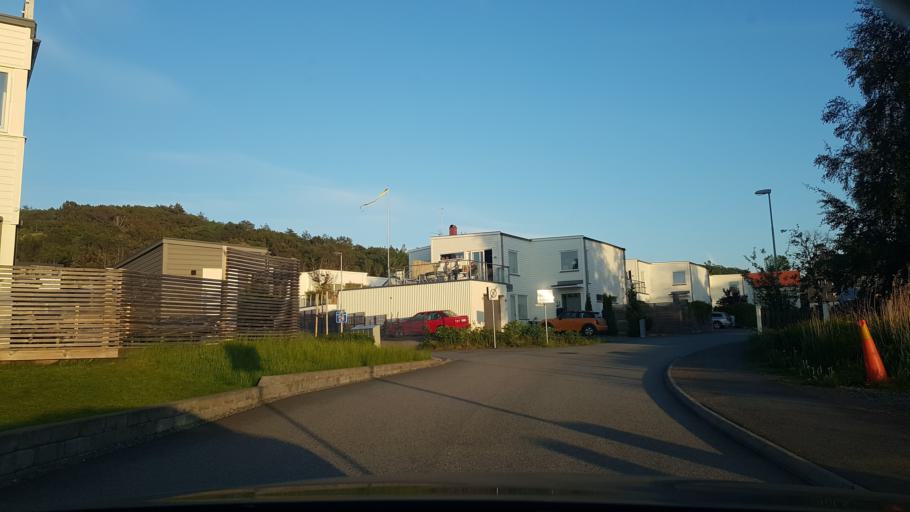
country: SE
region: Vaestra Goetaland
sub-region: Goteborg
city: Billdal
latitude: 57.5978
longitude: 11.9259
